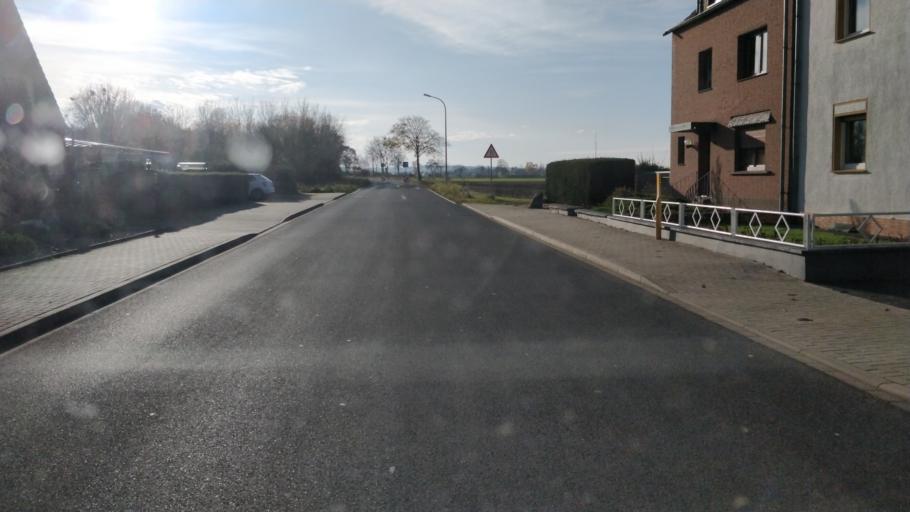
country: DE
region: North Rhine-Westphalia
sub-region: Regierungsbezirk Koln
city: Rheinbach
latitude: 50.6451
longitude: 6.8777
